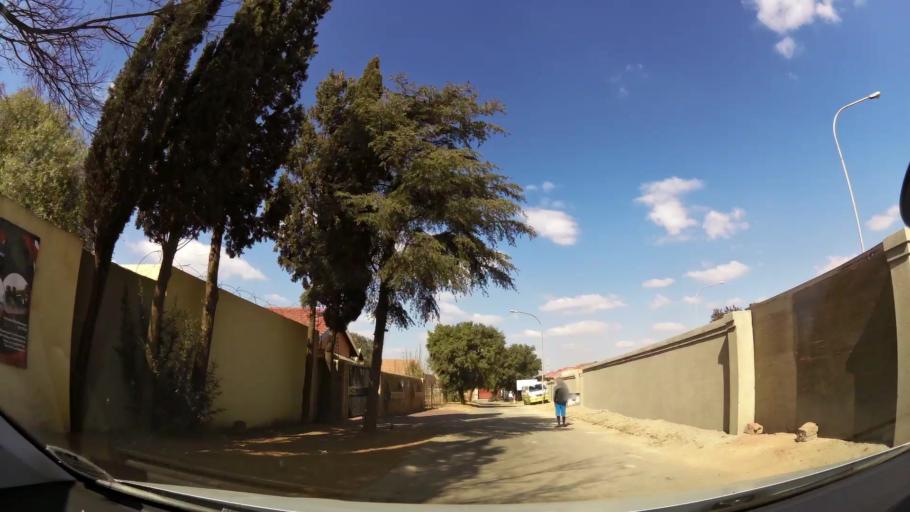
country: ZA
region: Gauteng
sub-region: City of Johannesburg Metropolitan Municipality
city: Roodepoort
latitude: -26.2100
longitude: 27.8706
